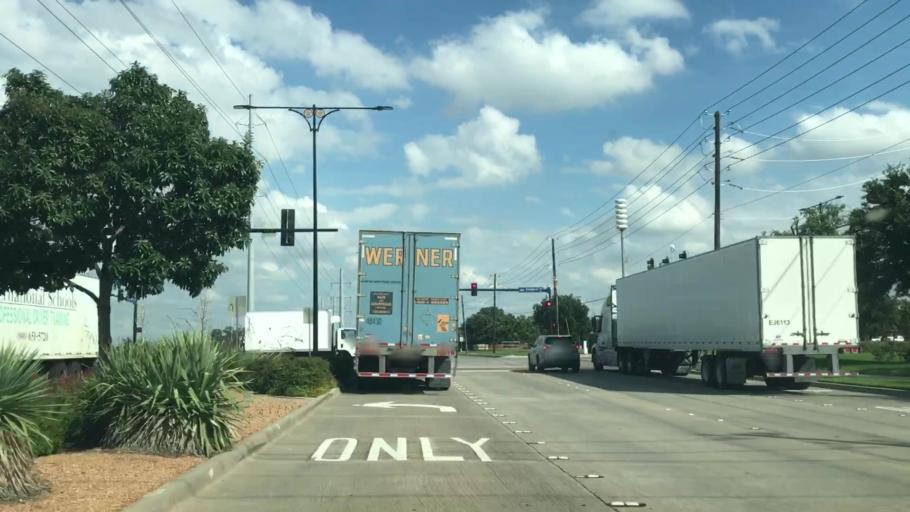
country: US
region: Texas
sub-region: Dallas County
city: Coppell
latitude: 32.9731
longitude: -97.0157
